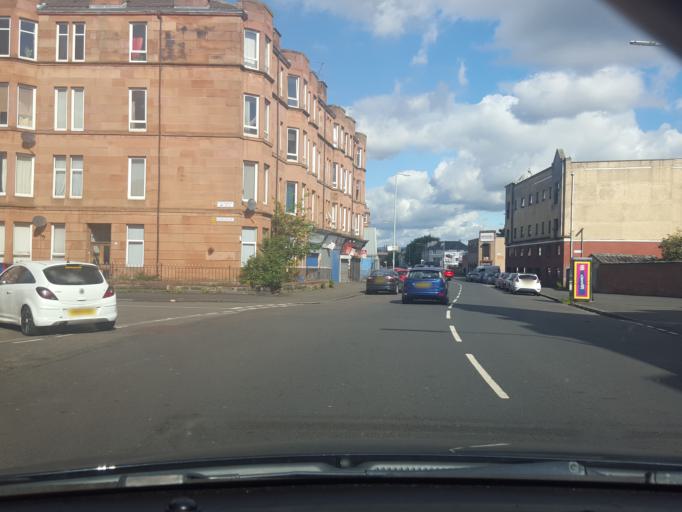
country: GB
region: Scotland
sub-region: Glasgow City
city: Glasgow
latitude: 55.8527
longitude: -4.3059
